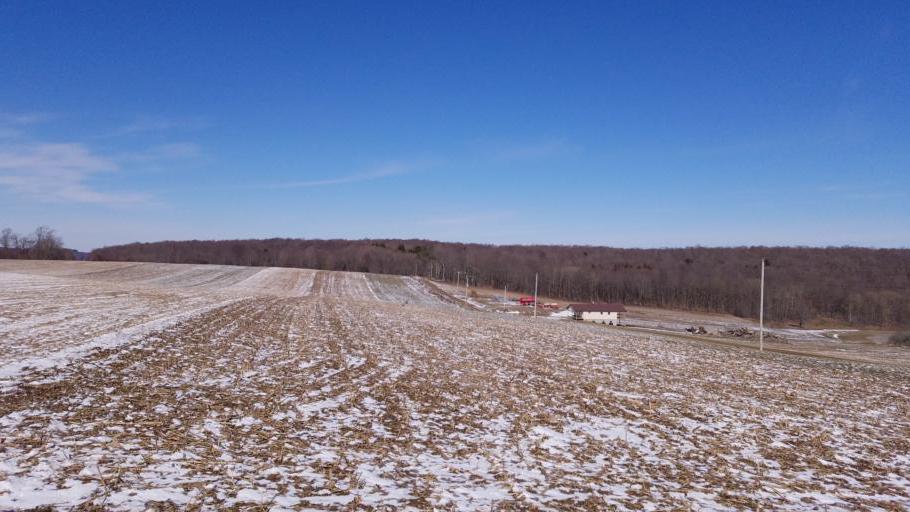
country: US
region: New York
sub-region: Allegany County
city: Wellsville
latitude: 42.0004
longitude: -77.9309
